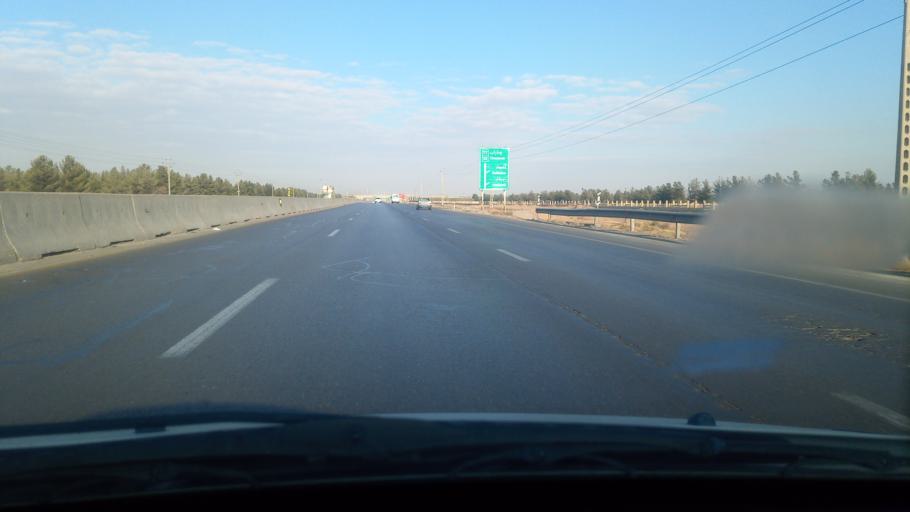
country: IR
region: Razavi Khorasan
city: Chenaran
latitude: 36.5783
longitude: 59.2229
